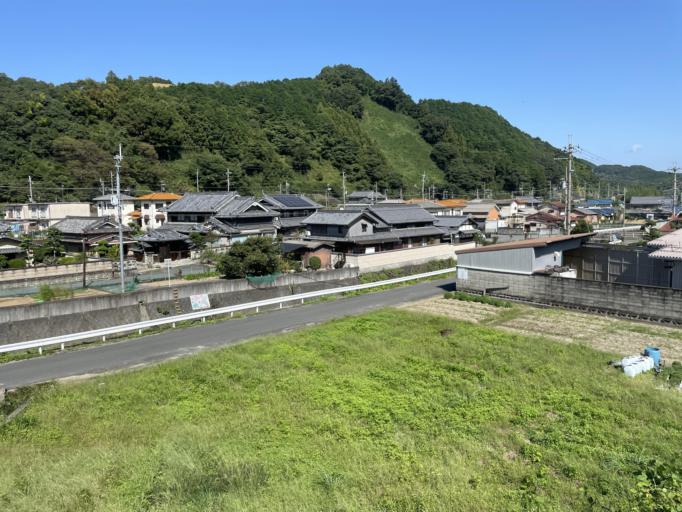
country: JP
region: Nara
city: Gose
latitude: 34.4255
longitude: 135.7546
